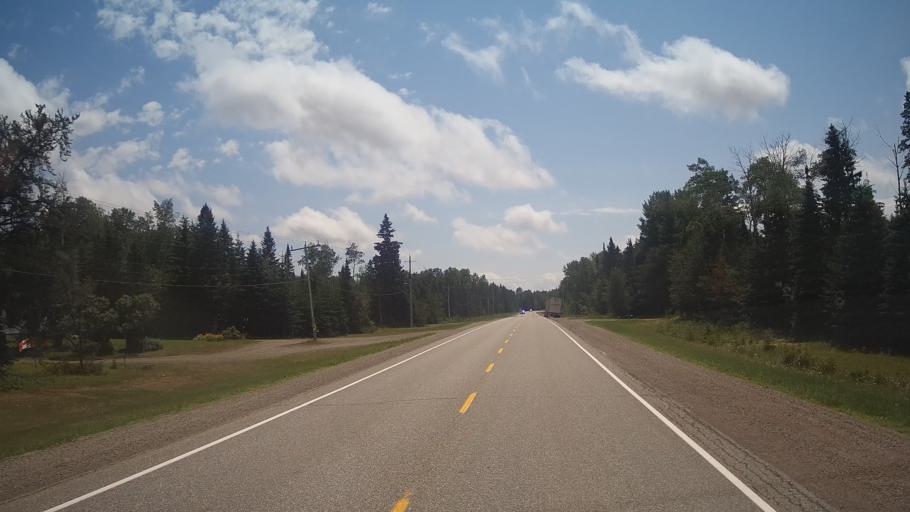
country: CA
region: Ontario
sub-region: Thunder Bay District
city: Thunder Bay
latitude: 48.9106
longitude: -88.3710
